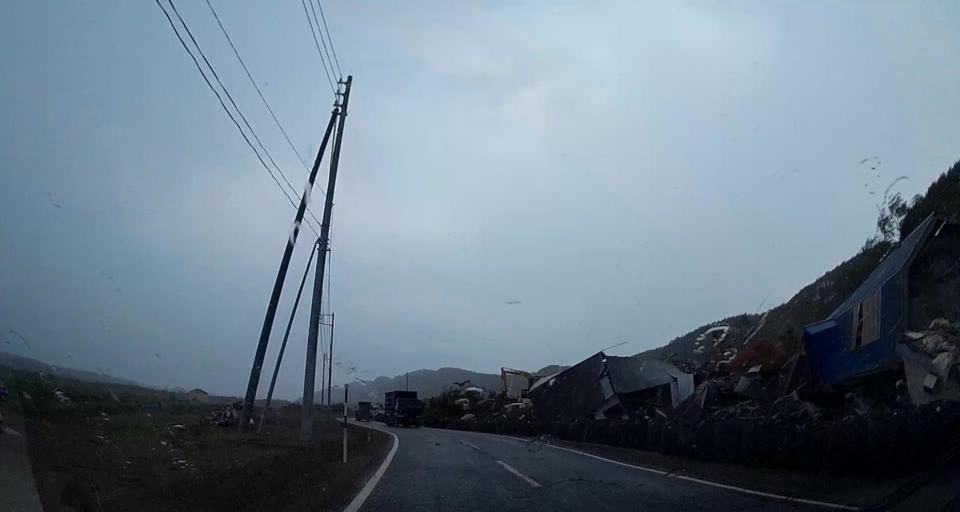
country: JP
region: Hokkaido
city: Chitose
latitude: 42.7506
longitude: 141.9131
